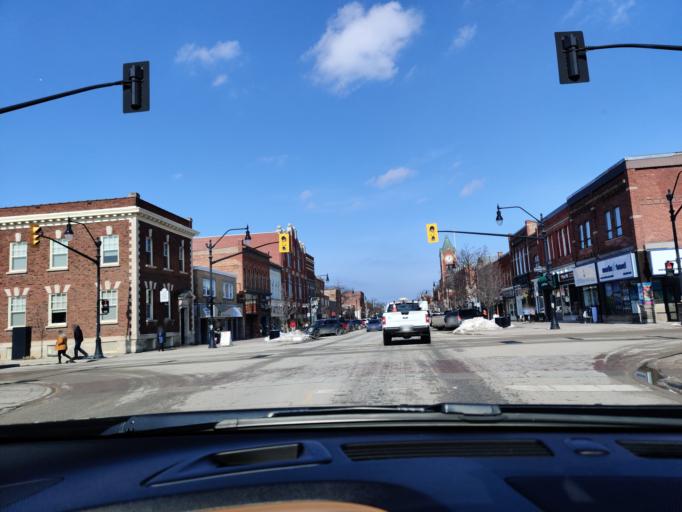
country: CA
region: Ontario
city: Collingwood
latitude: 44.4987
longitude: -80.2166
